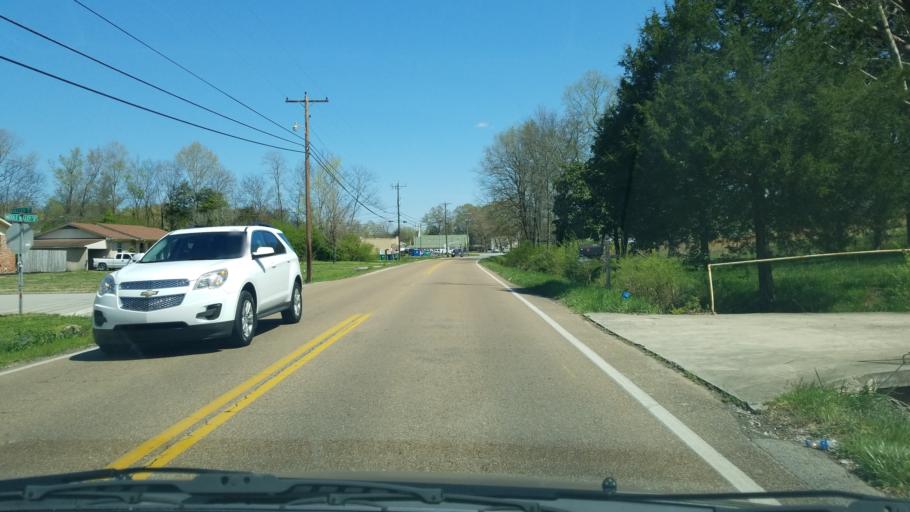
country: US
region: Tennessee
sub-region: Hamilton County
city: Middle Valley
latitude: 35.1868
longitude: -85.1925
